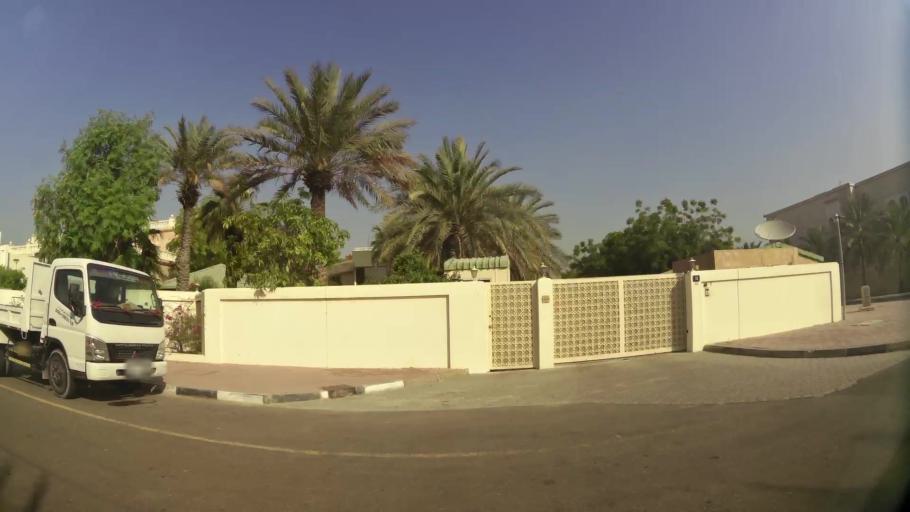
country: AE
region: Ash Shariqah
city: Sharjah
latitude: 25.3109
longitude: 55.3453
